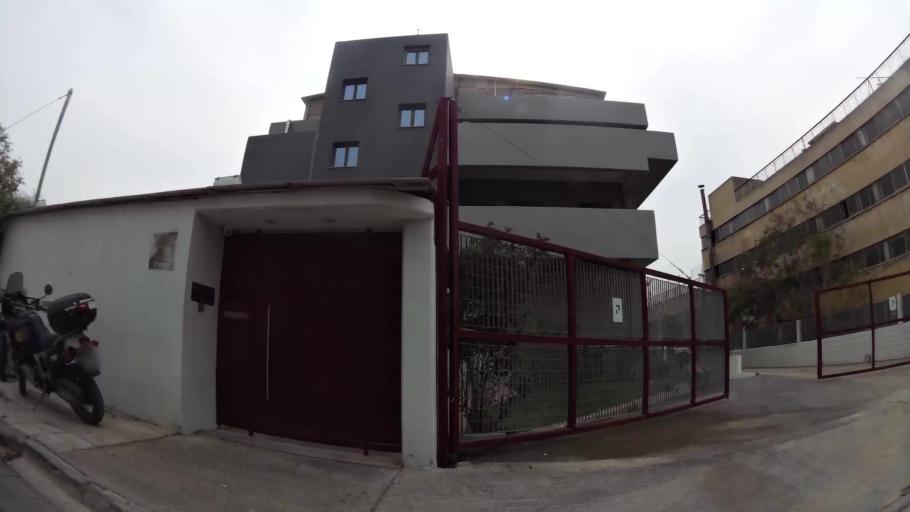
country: GR
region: Attica
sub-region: Nomarchia Athinas
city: Moskhaton
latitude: 37.9593
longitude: 23.6788
